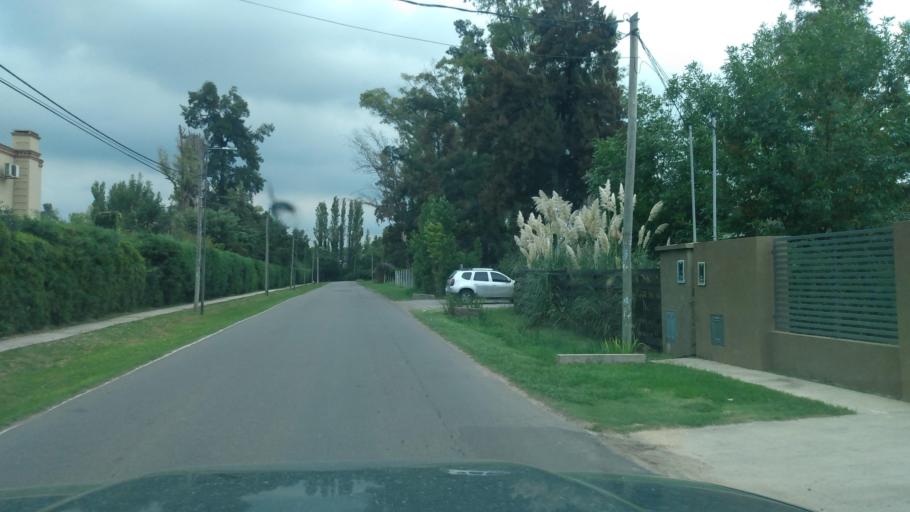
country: AR
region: Buenos Aires
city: Hurlingham
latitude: -34.5754
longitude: -58.7004
